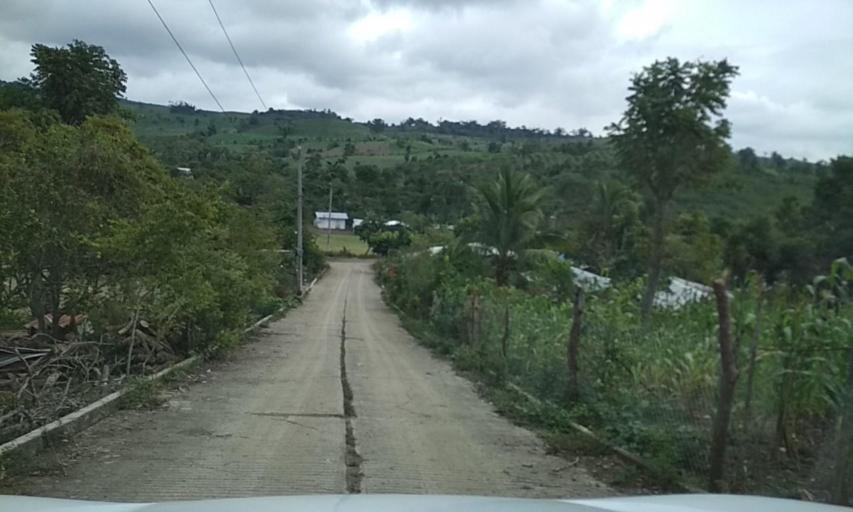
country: MX
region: Veracruz
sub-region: Coatzintla
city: Manuel Maria Contreras
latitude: 20.3502
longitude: -97.4697
